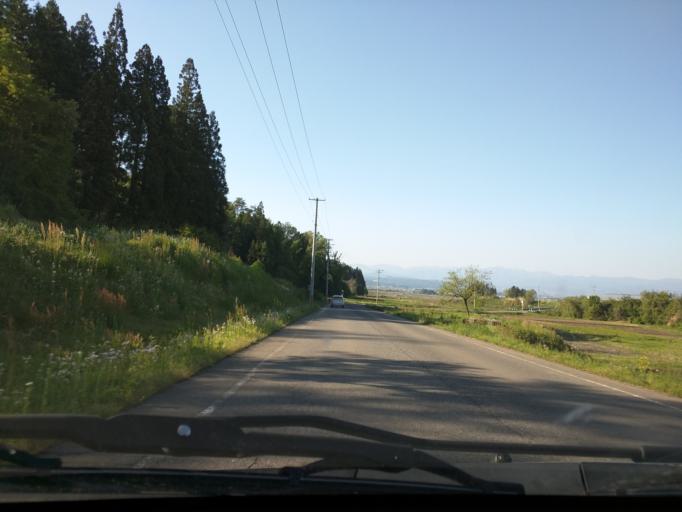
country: JP
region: Fukushima
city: Kitakata
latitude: 37.5201
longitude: 139.7979
